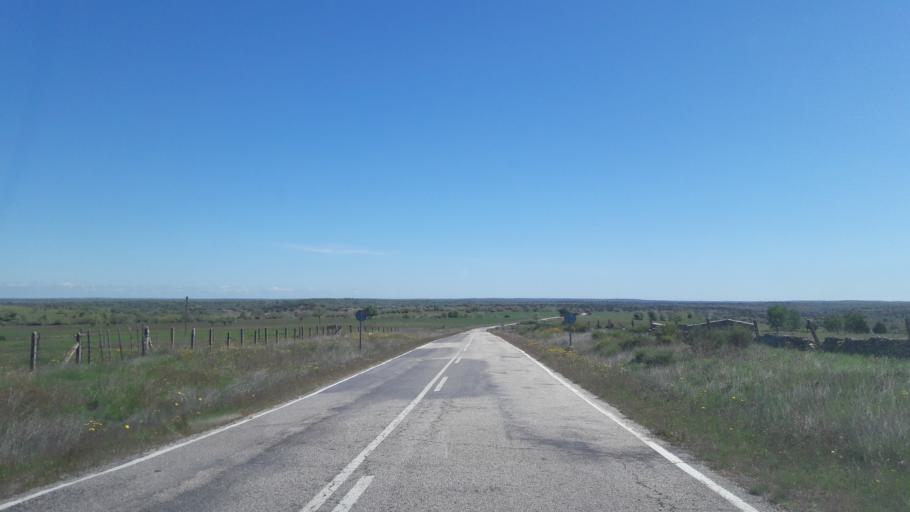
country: ES
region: Castille and Leon
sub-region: Provincia de Salamanca
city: Vitigudino
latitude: 41.0198
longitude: -6.4178
